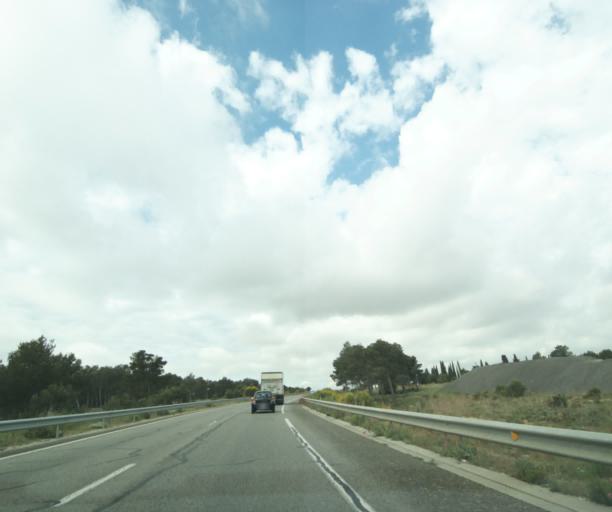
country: FR
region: Provence-Alpes-Cote d'Azur
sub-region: Departement des Bouches-du-Rhone
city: Les Pennes-Mirabeau
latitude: 43.4524
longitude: 5.3073
